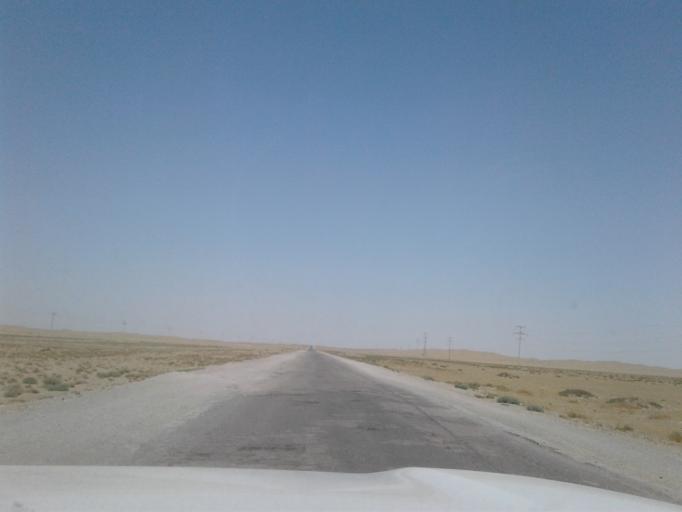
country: TM
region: Balkan
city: Gumdag
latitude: 38.3662
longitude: 54.3843
